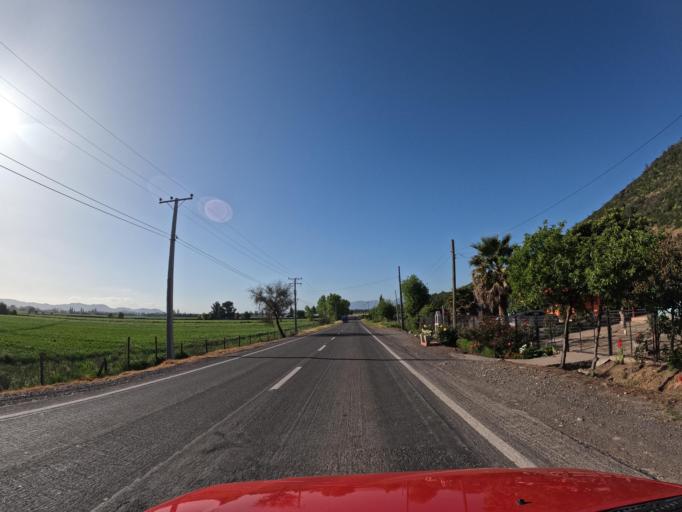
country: CL
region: Maule
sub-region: Provincia de Curico
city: Teno
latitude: -34.7779
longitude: -71.2308
